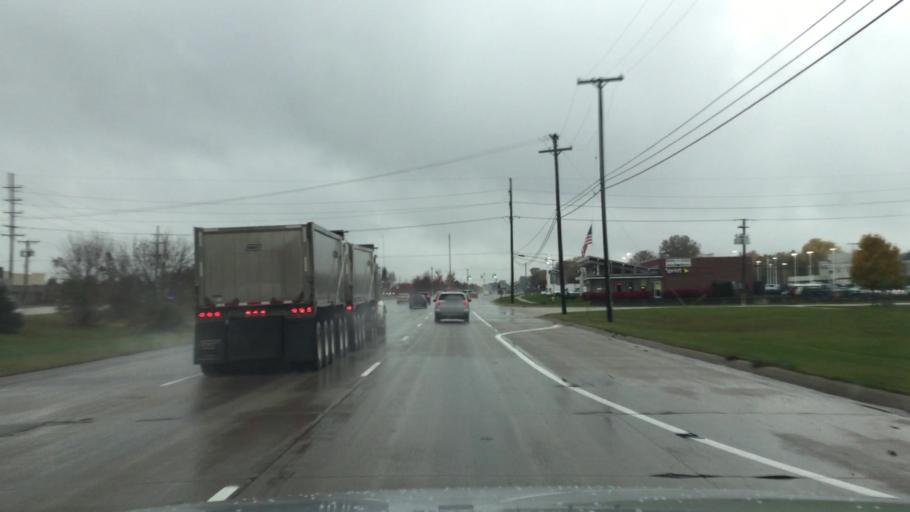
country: US
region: Michigan
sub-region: Macomb County
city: Mount Clemens
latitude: 42.6304
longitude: -82.8547
